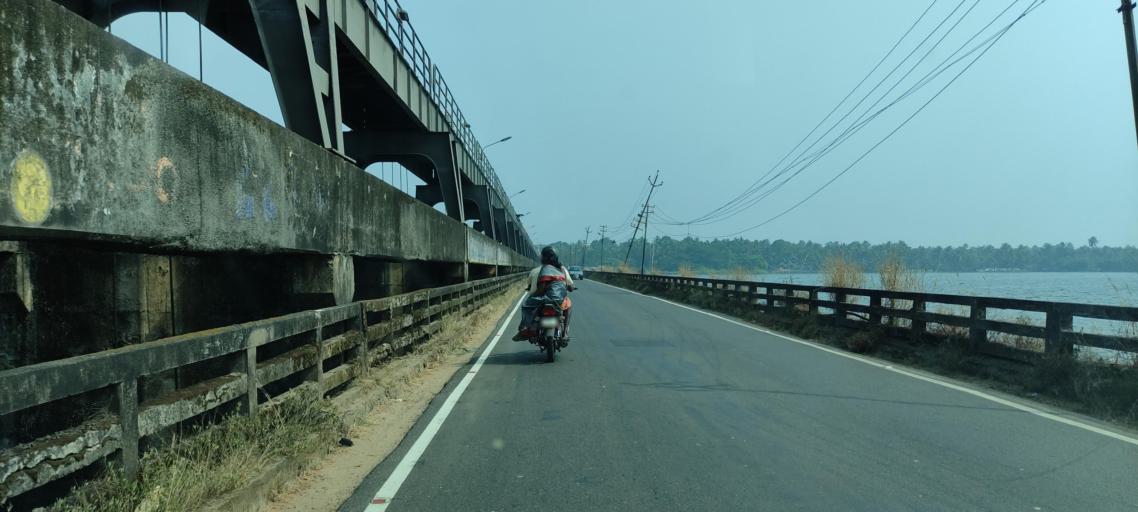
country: IN
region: Kerala
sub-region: Alappuzha
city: Shertallai
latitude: 9.6733
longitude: 76.4024
